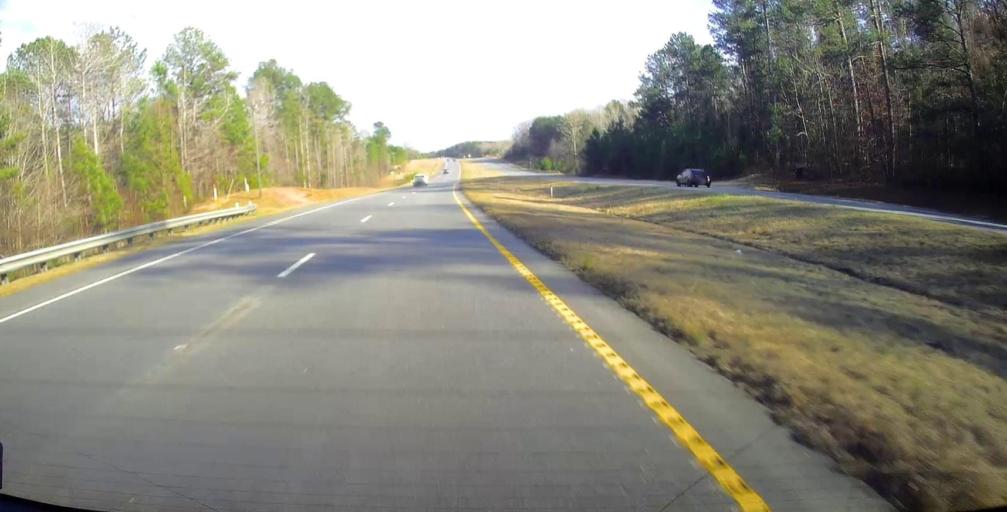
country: US
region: Georgia
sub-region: Talbot County
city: Talbotton
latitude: 32.5657
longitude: -84.6300
